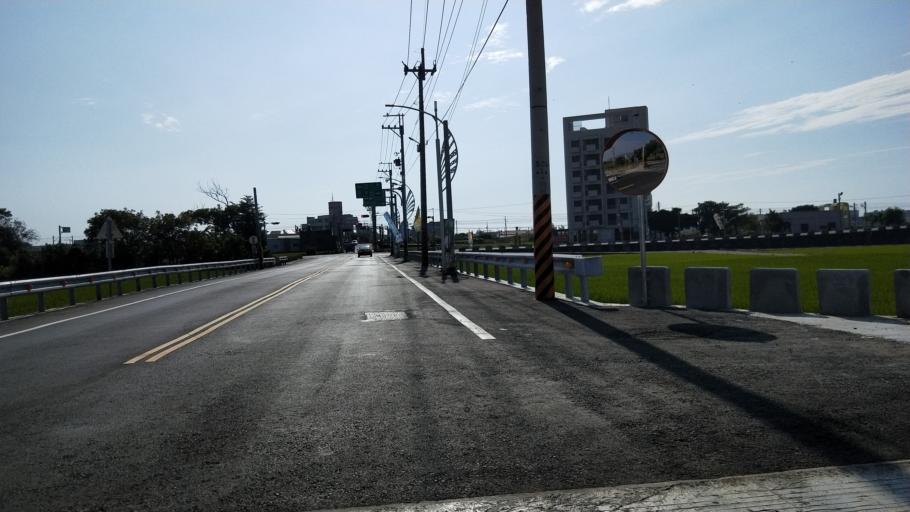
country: TW
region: Taiwan
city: Fengyuan
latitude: 24.4197
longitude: 120.6562
